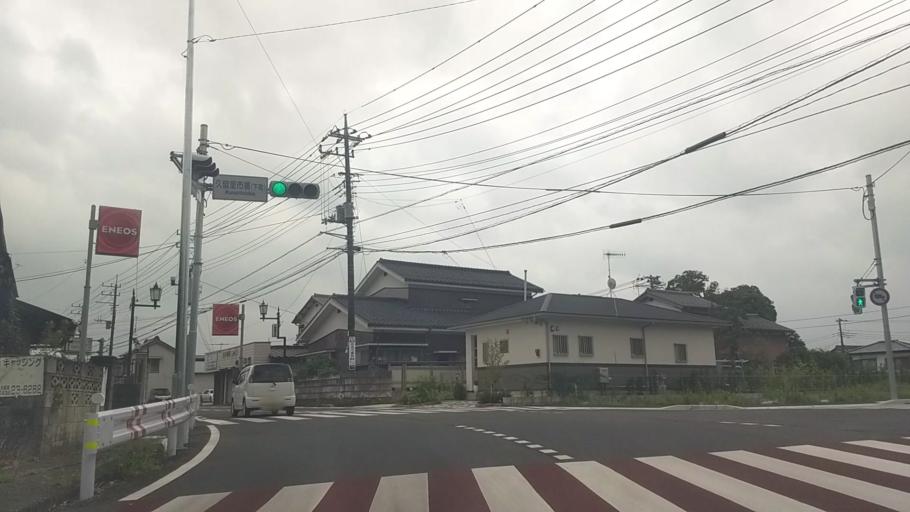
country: JP
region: Chiba
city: Kisarazu
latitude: 35.2989
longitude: 140.0750
